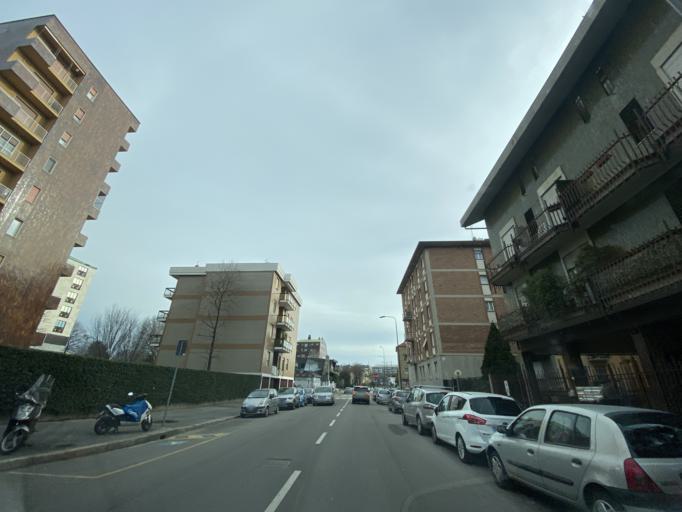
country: IT
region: Lombardy
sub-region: Citta metropolitana di Milano
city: Milano
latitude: 45.4930
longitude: 9.1977
